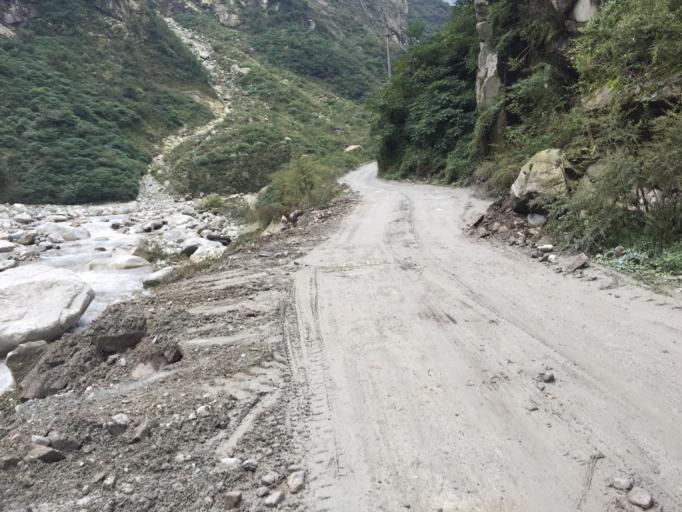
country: CN
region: Sichuan
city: Guangsheng
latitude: 31.0683
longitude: 103.4438
